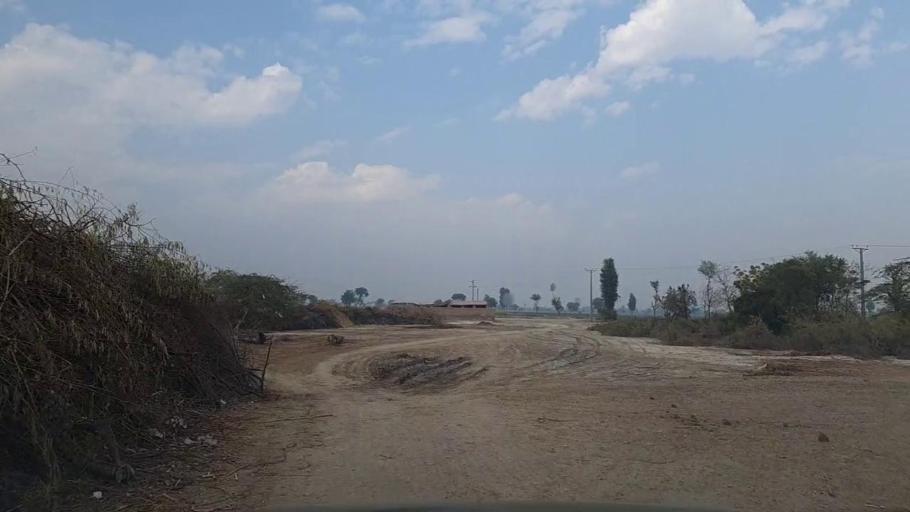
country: PK
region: Sindh
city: Daur
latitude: 26.3734
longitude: 68.3895
